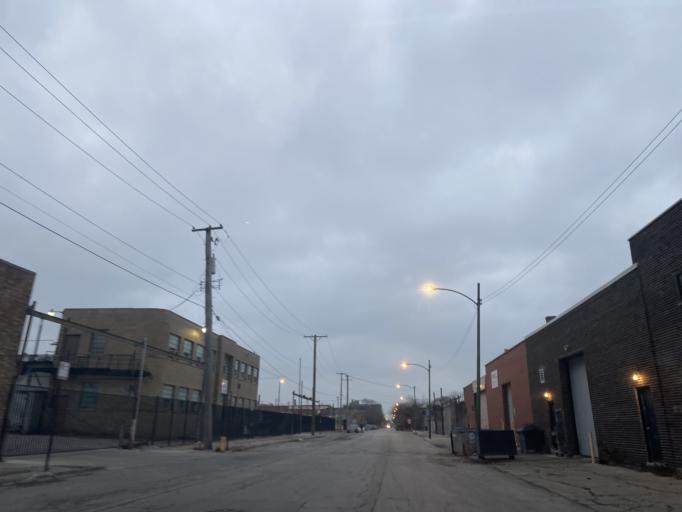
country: US
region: Illinois
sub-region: Cook County
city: Chicago
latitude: 41.8897
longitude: -87.6778
